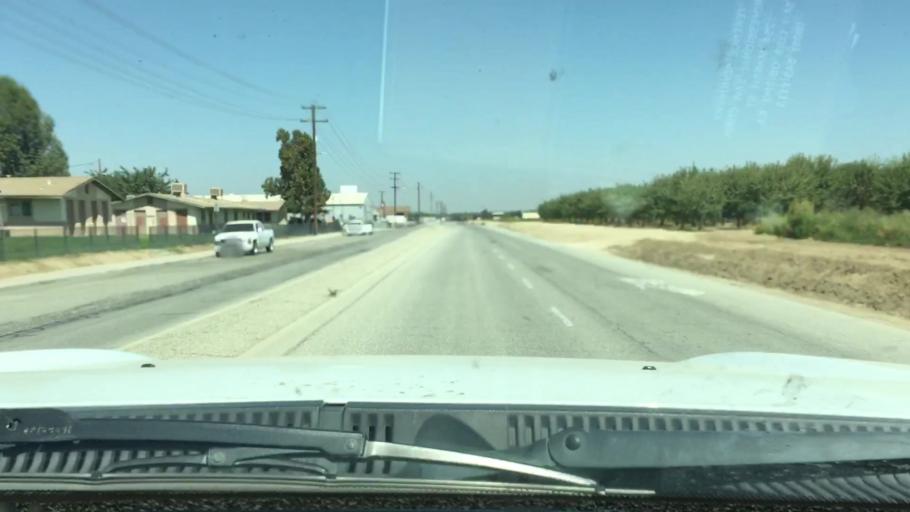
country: US
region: California
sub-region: Kern County
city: Wasco
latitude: 35.5938
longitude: -119.3282
